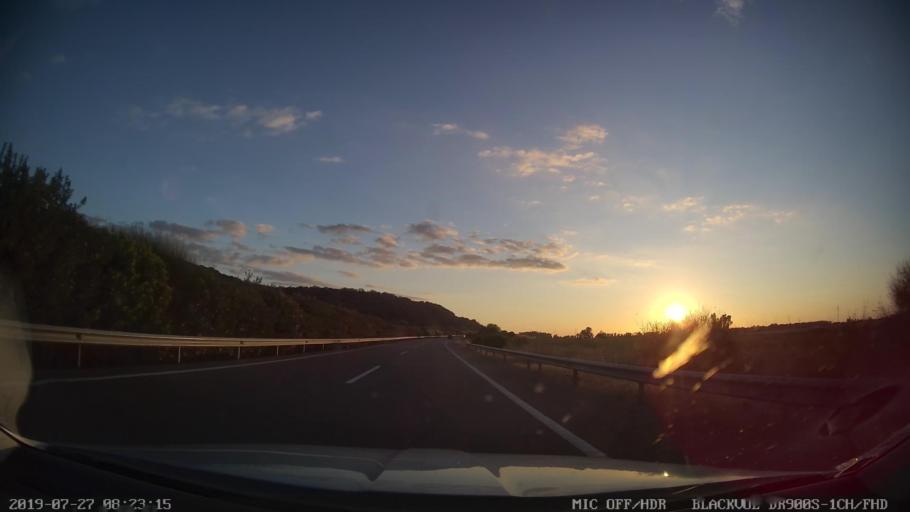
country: ES
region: Extremadura
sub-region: Provincia de Badajoz
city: Torremayor
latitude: 38.8595
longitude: -6.5645
